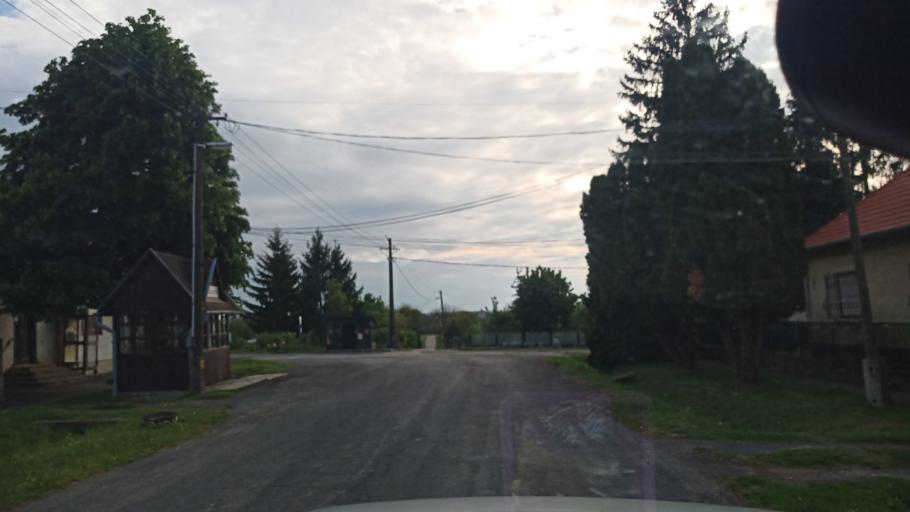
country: HU
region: Zala
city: Pacsa
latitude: 46.7471
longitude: 17.0096
